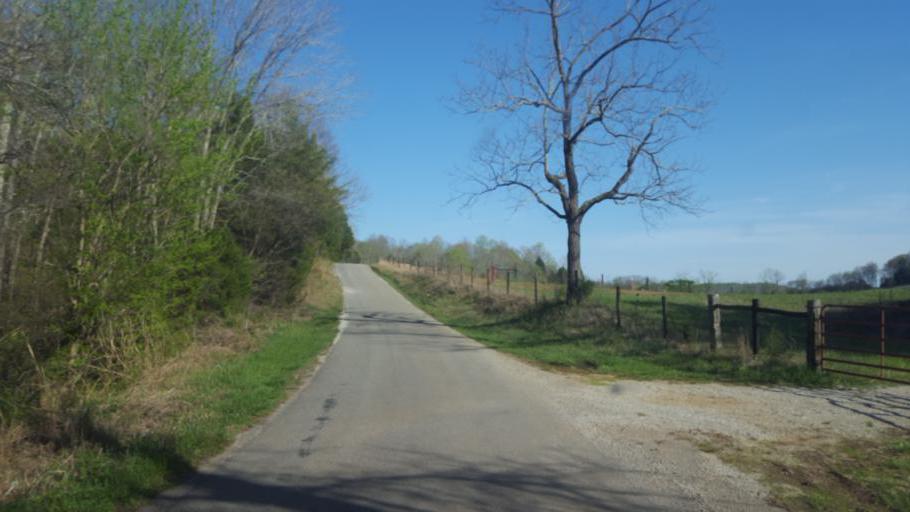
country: US
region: Kentucky
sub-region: Barren County
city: Cave City
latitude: 37.2011
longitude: -86.0179
